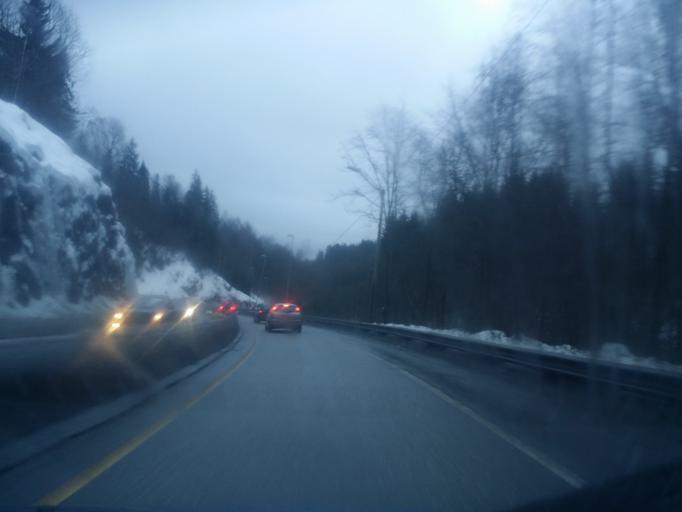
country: NO
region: Akershus
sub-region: Baerum
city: Skui
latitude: 59.9385
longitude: 10.4110
